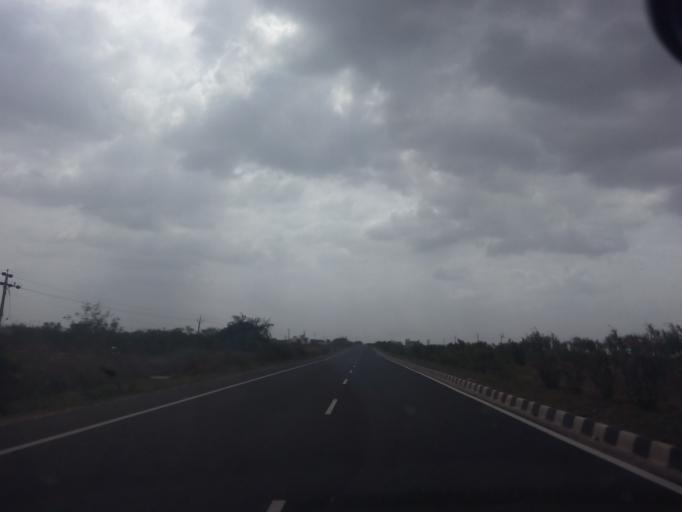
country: IN
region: Gujarat
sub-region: Surendranagar
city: Halvad
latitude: 23.0052
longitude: 71.0978
